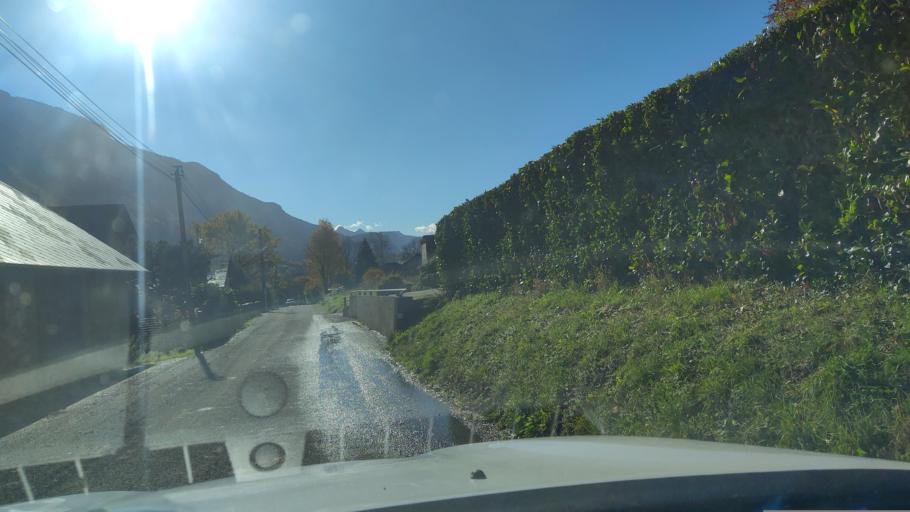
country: FR
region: Rhone-Alpes
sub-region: Departement de la Savoie
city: Vimines
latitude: 45.5118
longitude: 5.8432
